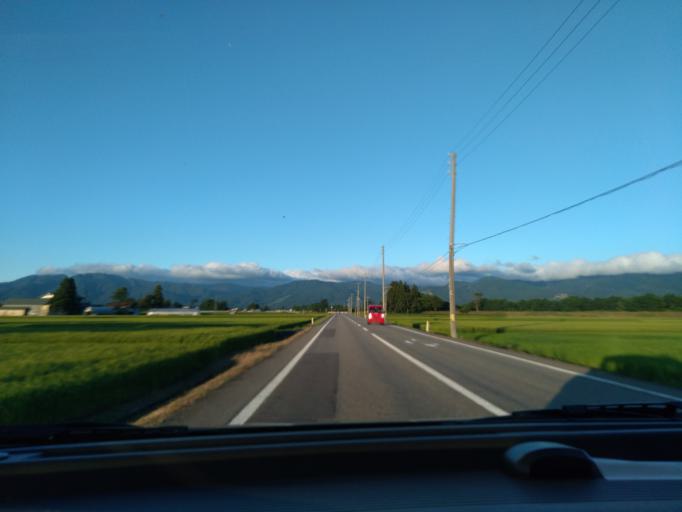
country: JP
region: Akita
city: Omagari
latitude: 39.4879
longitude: 140.5528
